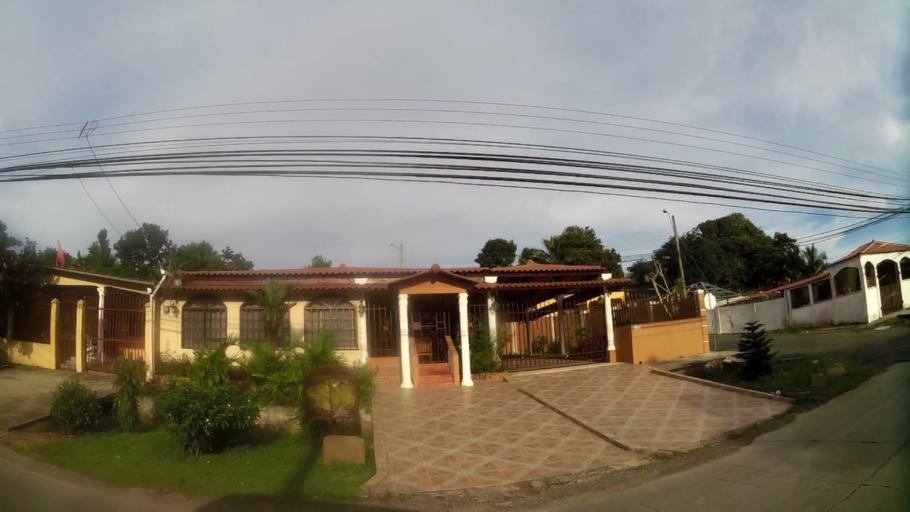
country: PA
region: Panama
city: La Chorrera
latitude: 8.8956
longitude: -79.7662
